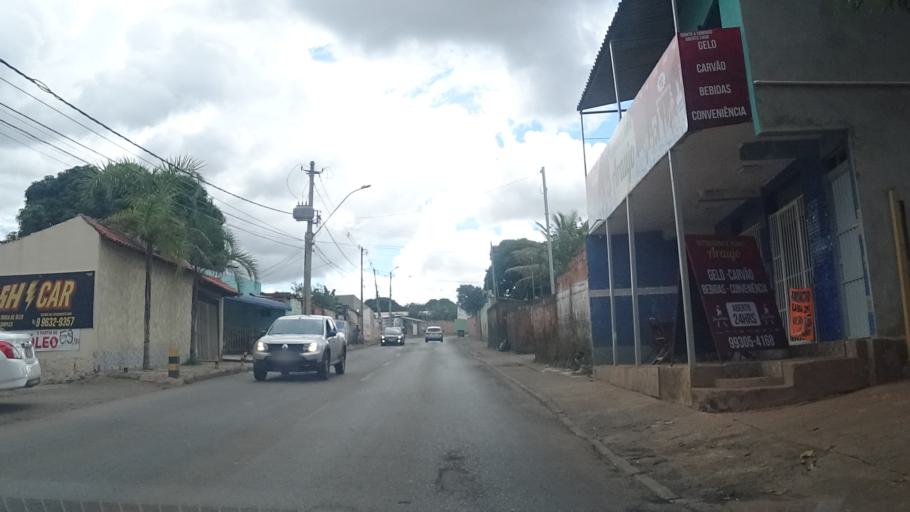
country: BR
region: Federal District
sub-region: Brasilia
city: Brasilia
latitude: -15.8484
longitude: -48.0263
